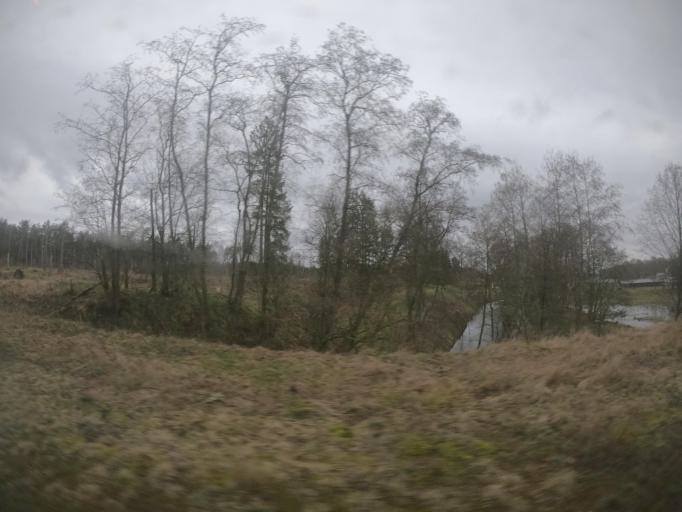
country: PL
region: West Pomeranian Voivodeship
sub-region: Powiat szczecinecki
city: Bialy Bor
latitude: 53.8318
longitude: 16.8745
